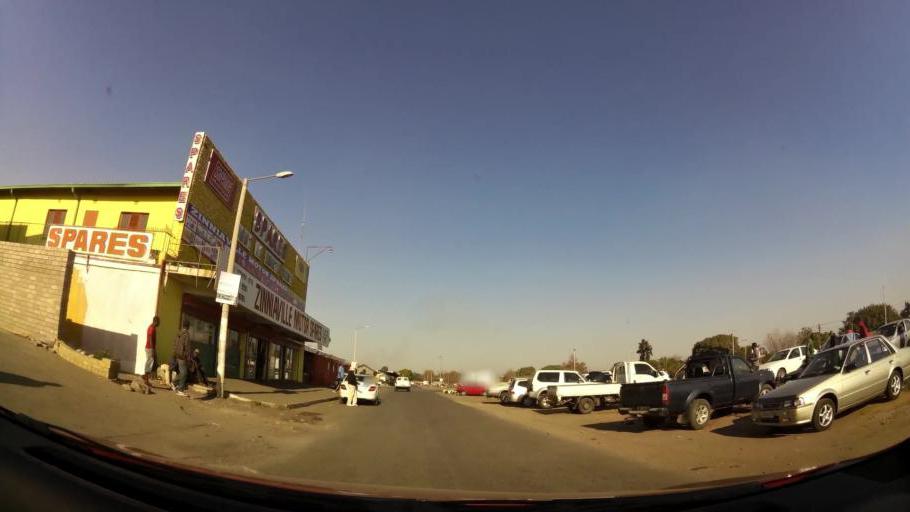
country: ZA
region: North-West
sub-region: Bojanala Platinum District Municipality
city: Rustenburg
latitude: -25.6491
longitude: 27.2382
